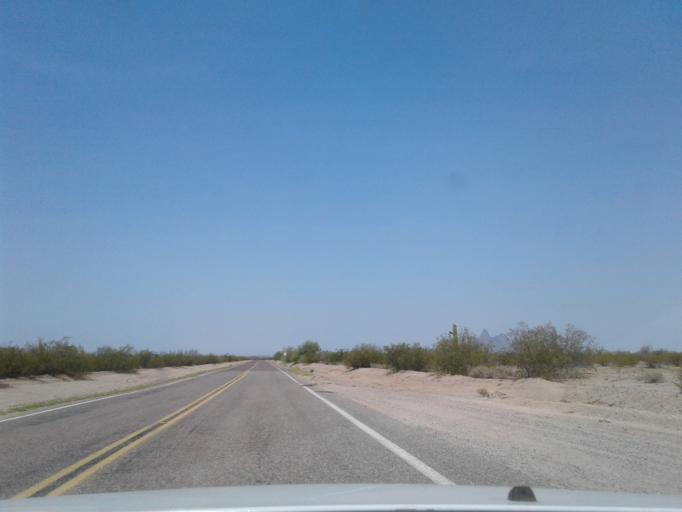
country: US
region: Arizona
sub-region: Pima County
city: Marana
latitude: 32.6164
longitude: -111.2614
